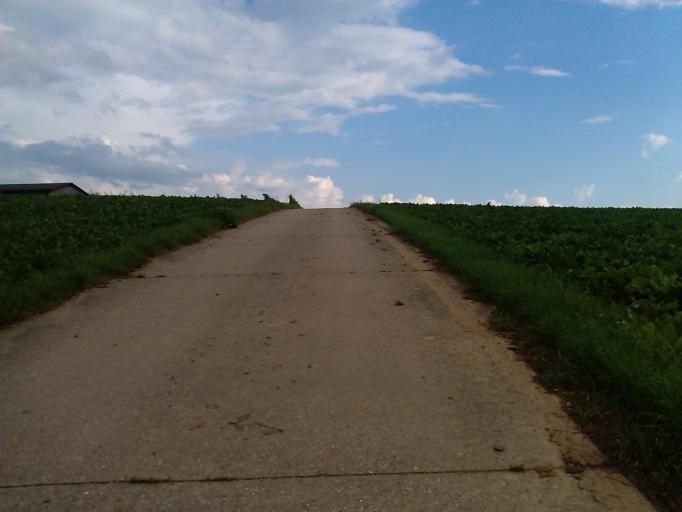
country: DE
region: Baden-Wuerttemberg
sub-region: Regierungsbezirk Stuttgart
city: Neckarwestheim
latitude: 49.0572
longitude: 9.1692
